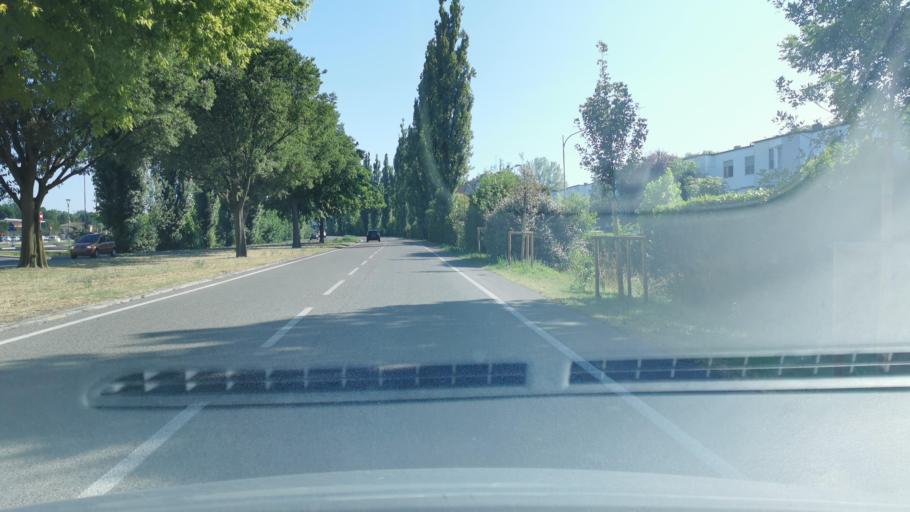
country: IT
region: Emilia-Romagna
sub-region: Provincia di Modena
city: Carpi Centro
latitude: 44.7770
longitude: 10.8642
